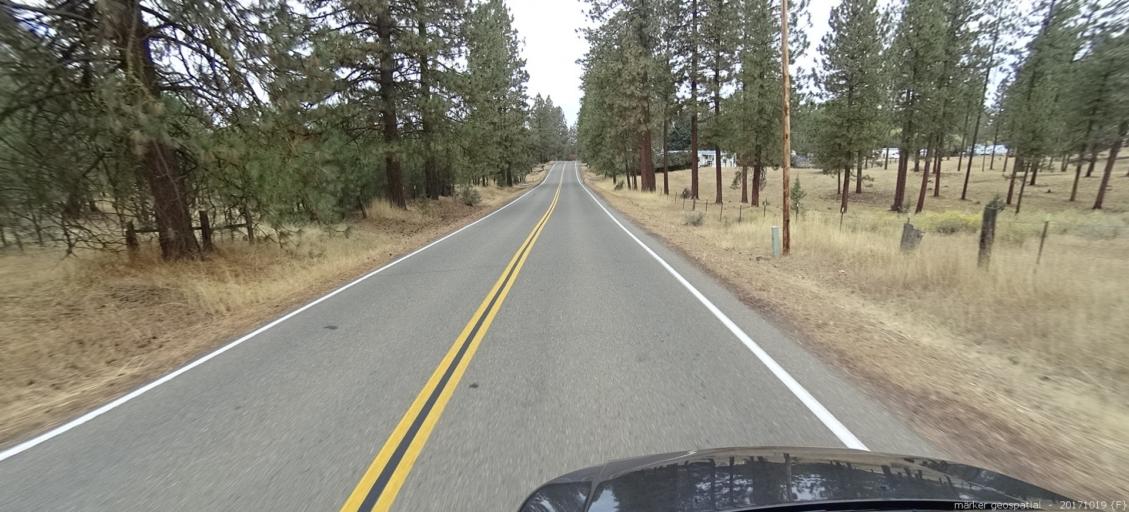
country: US
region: California
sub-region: Shasta County
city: Burney
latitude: 41.0572
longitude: -121.3689
